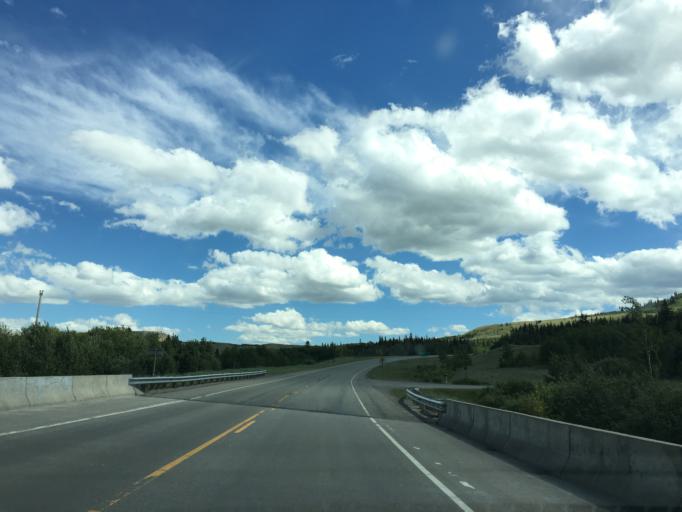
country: US
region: Montana
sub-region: Glacier County
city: Browning
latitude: 48.6085
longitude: -113.2871
